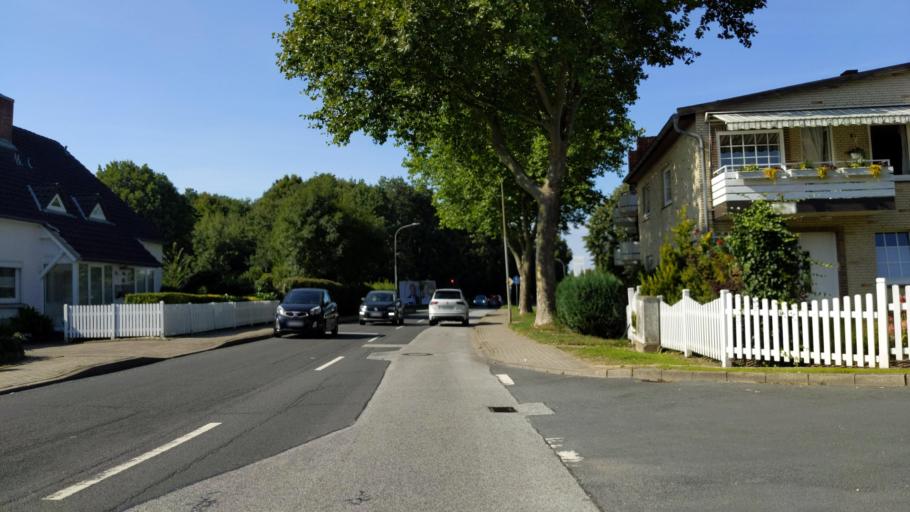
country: DE
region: Schleswig-Holstein
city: Stockelsdorf
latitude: 53.9012
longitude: 10.6440
